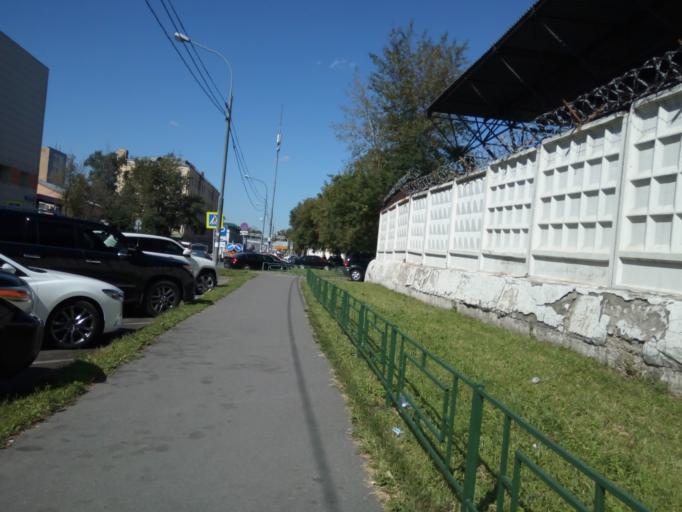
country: RU
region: Moscow
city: Sokol
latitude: 55.7705
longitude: 37.5204
